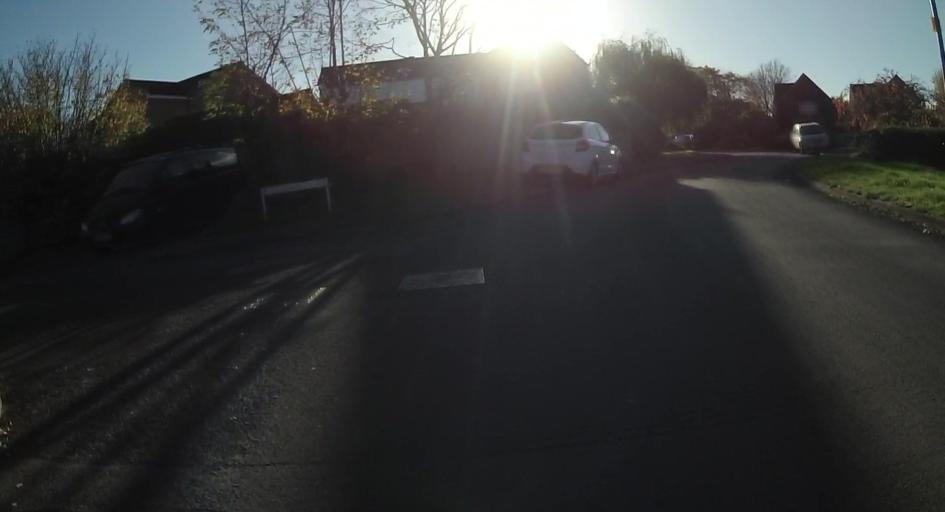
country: GB
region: England
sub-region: Wokingham
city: Barkham
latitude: 51.4093
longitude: -0.8600
